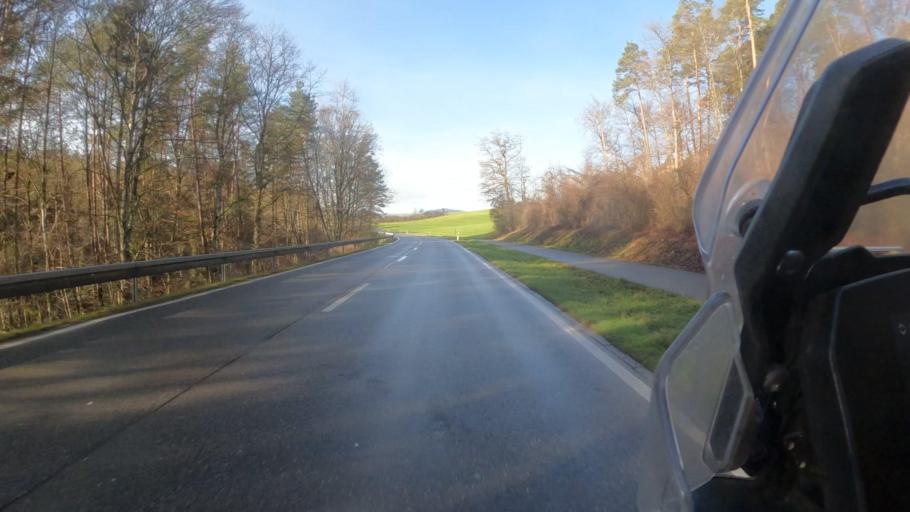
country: DE
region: Baden-Wuerttemberg
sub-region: Freiburg Region
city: Engen
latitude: 47.8531
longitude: 8.8110
